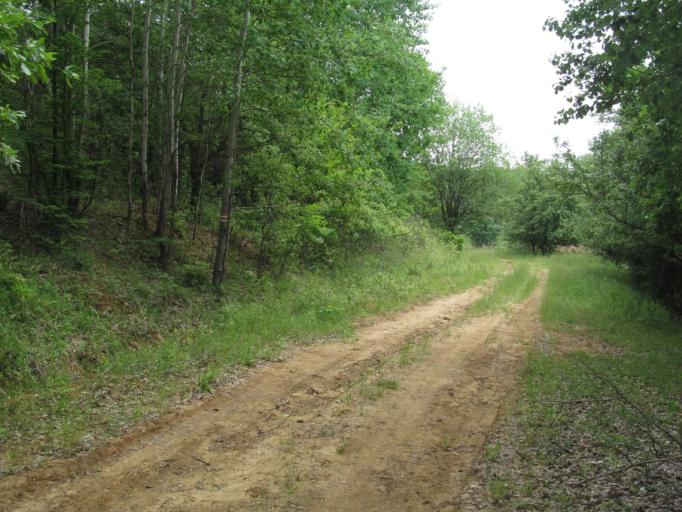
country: HU
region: Borsod-Abauj-Zemplen
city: Jardanhaza
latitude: 48.1721
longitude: 20.1597
